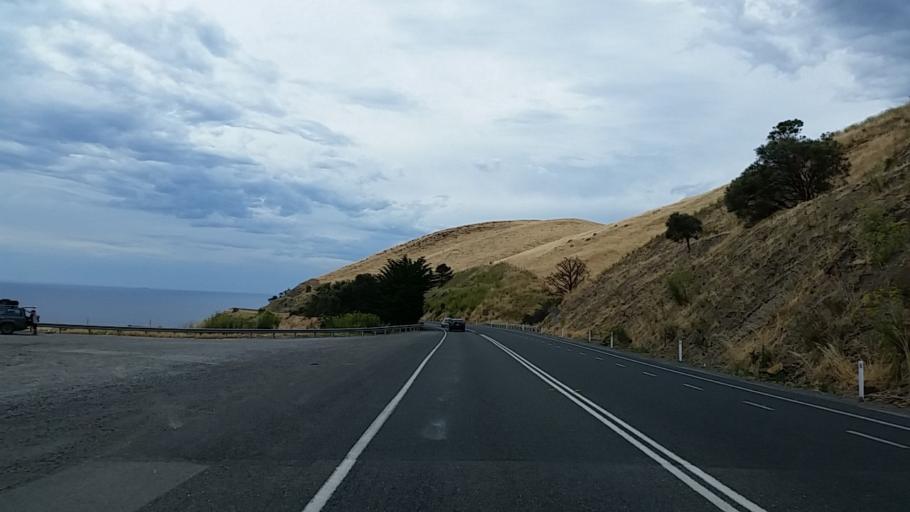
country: AU
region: South Australia
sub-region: Onkaparinga
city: Port Willunga
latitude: -35.3598
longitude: 138.4532
